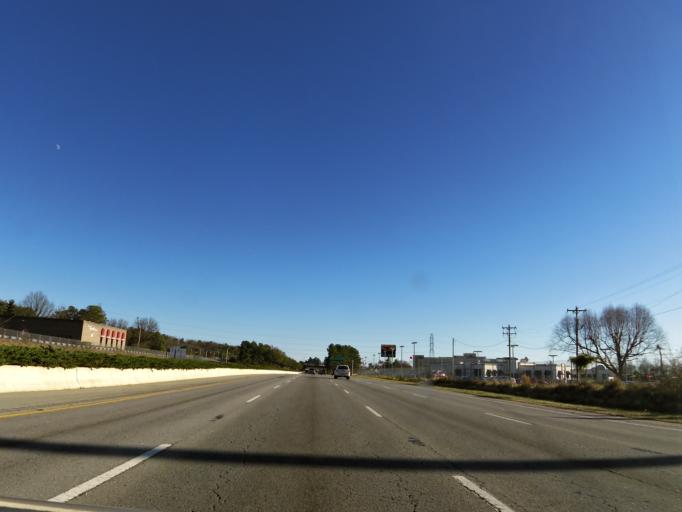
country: US
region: South Carolina
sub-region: Greenville County
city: Wade Hampton
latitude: 34.8429
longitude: -82.3185
